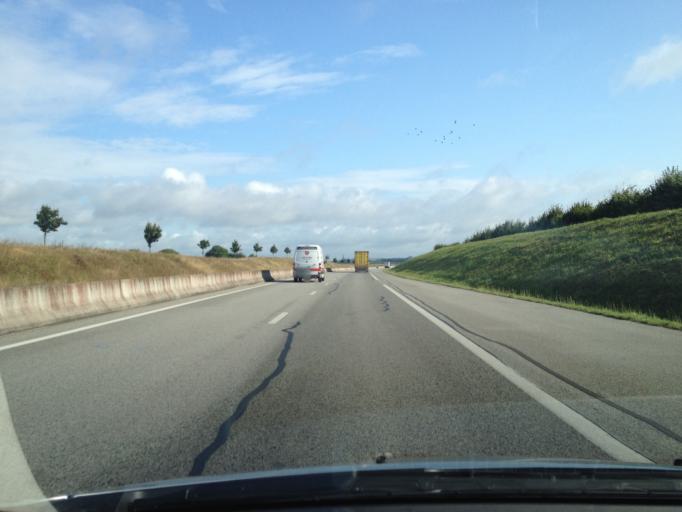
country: FR
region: Lower Normandy
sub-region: Departement de l'Orne
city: Sees
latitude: 48.5680
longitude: 0.1750
